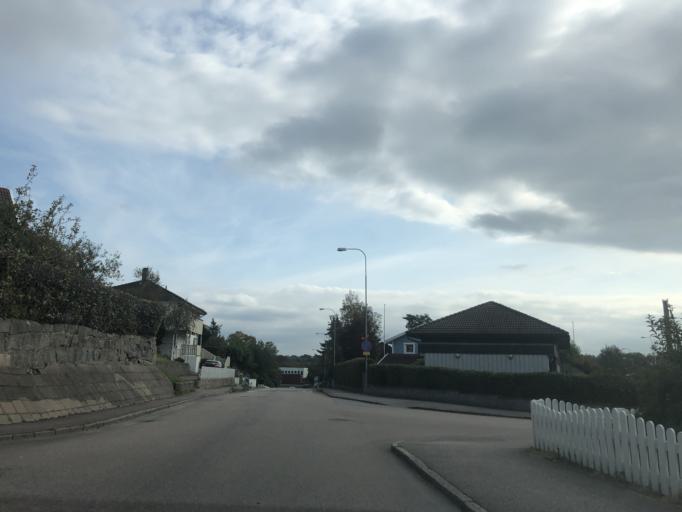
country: SE
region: Vaestra Goetaland
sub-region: Goteborg
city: Majorna
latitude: 57.6530
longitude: 11.8885
